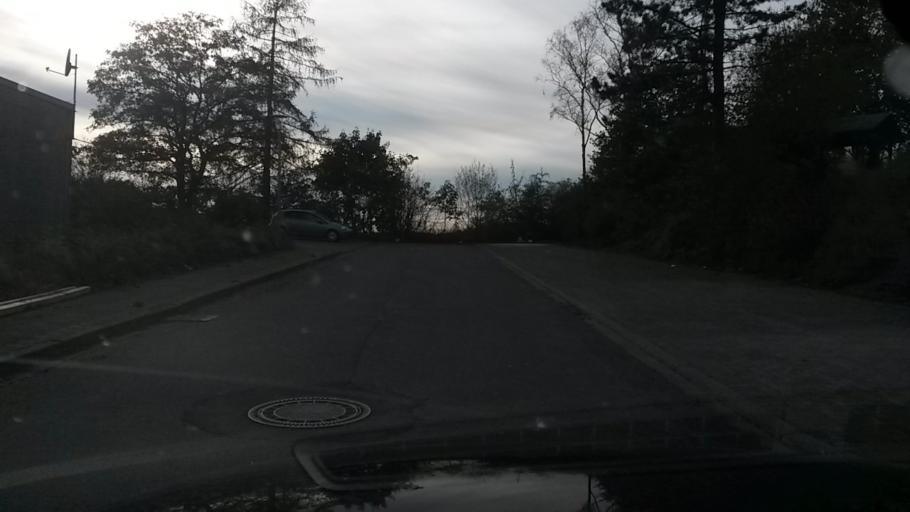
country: DE
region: North Rhine-Westphalia
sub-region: Regierungsbezirk Arnsberg
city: Herscheid
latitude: 51.1826
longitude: 7.7409
